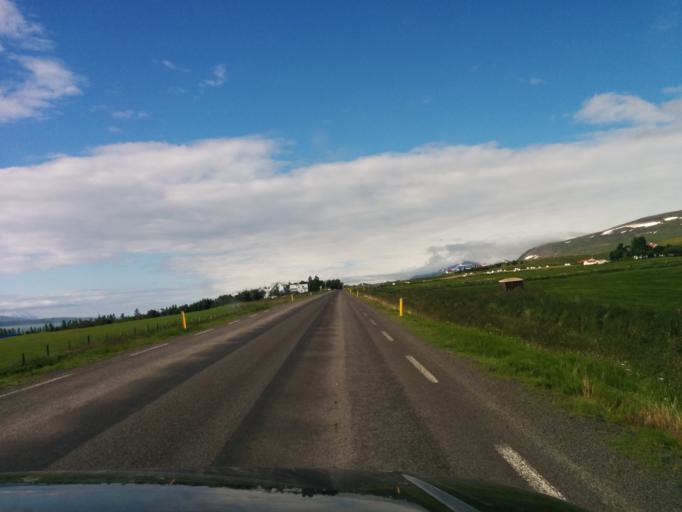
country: IS
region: Northeast
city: Akureyri
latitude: 65.7460
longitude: -18.0746
